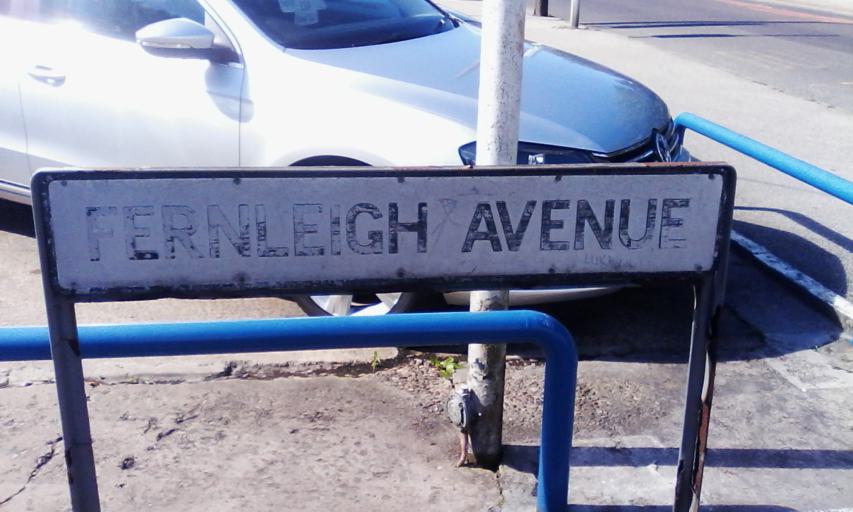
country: GB
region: England
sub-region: Nottinghamshire
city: Arnold
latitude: 52.9822
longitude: -1.1087
